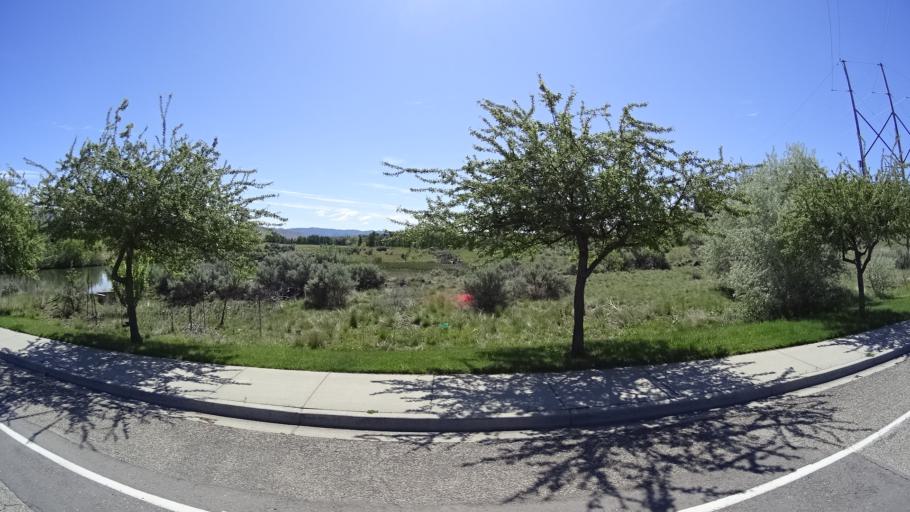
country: US
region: Idaho
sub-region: Ada County
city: Boise
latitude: 43.5462
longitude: -116.1537
